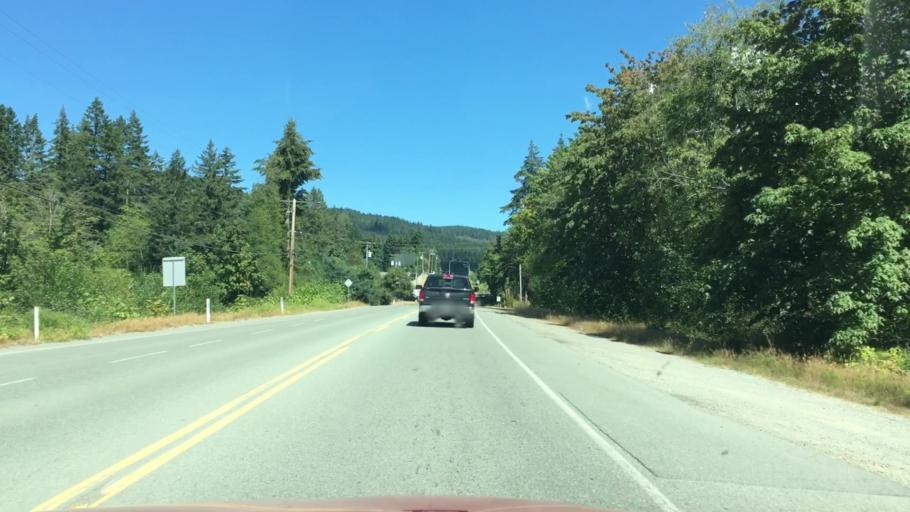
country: CA
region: British Columbia
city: Port Alberni
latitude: 49.2628
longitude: -124.7655
